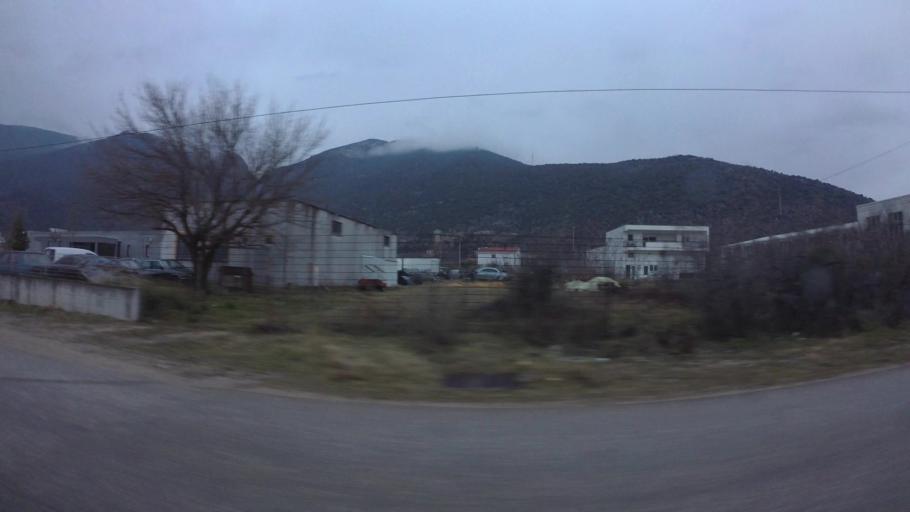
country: BA
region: Federation of Bosnia and Herzegovina
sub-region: Hercegovacko-Bosanski Kanton
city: Mostar
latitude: 43.3659
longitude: 17.8146
